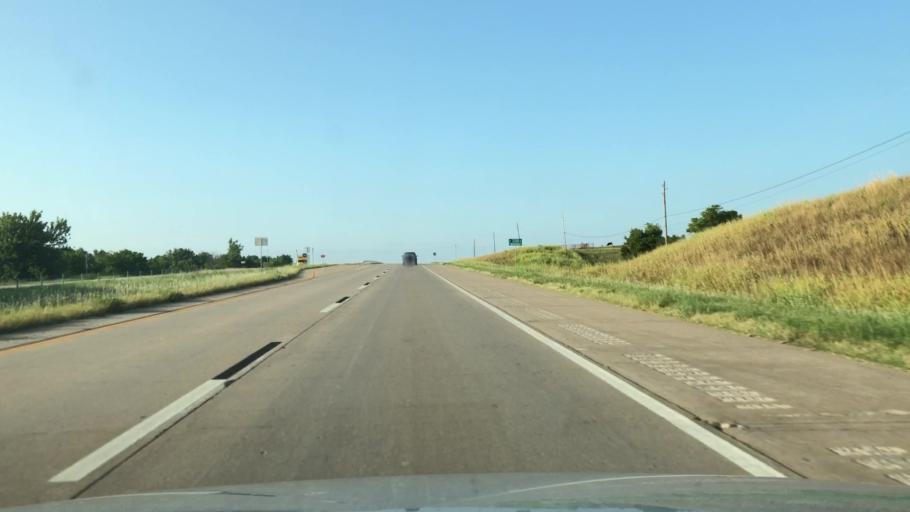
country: US
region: Oklahoma
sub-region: Osage County
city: Skiatook
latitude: 36.4828
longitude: -95.9207
